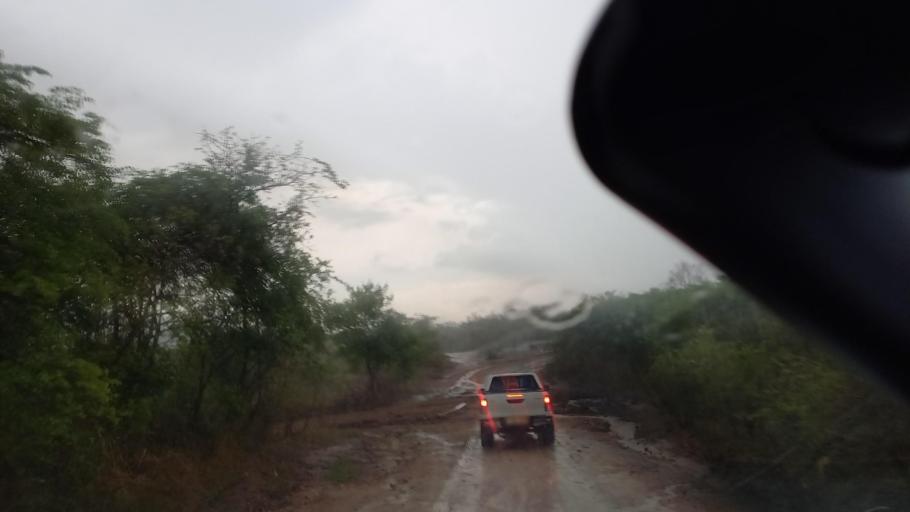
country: ZM
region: Lusaka
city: Kafue
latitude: -15.9346
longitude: 28.2095
